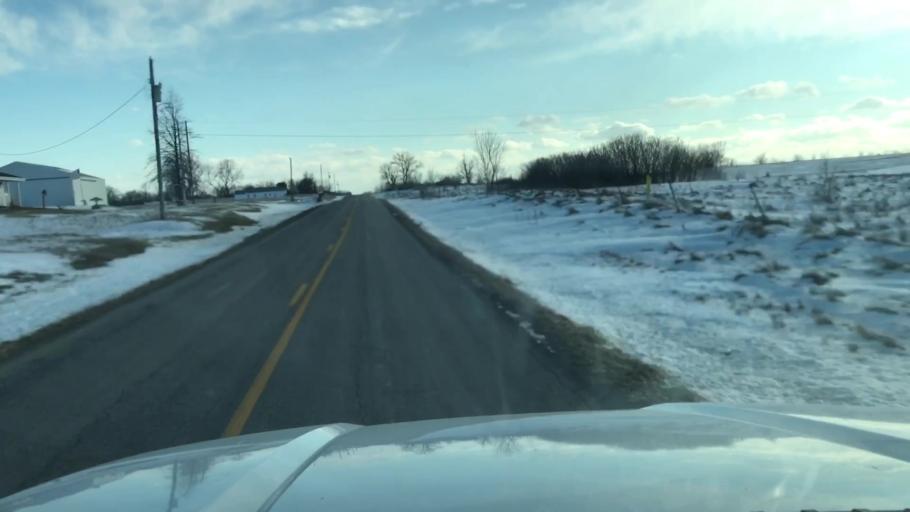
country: US
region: Missouri
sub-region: Holt County
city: Oregon
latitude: 40.1148
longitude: -95.0226
